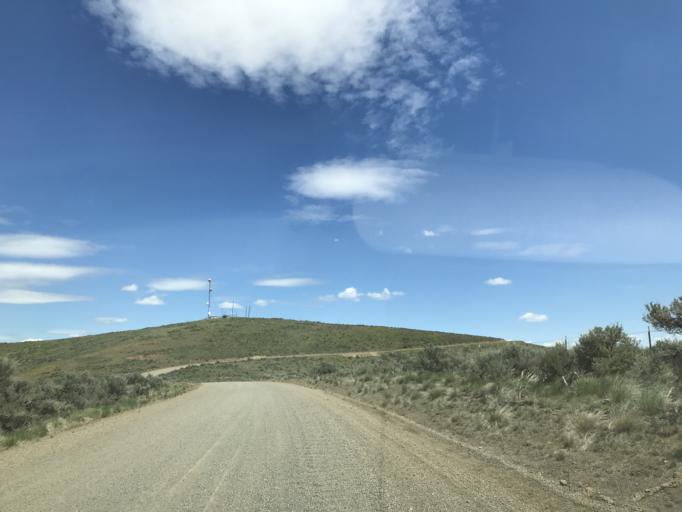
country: US
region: Washington
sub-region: Grant County
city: Quincy
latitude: 47.3175
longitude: -119.8077
